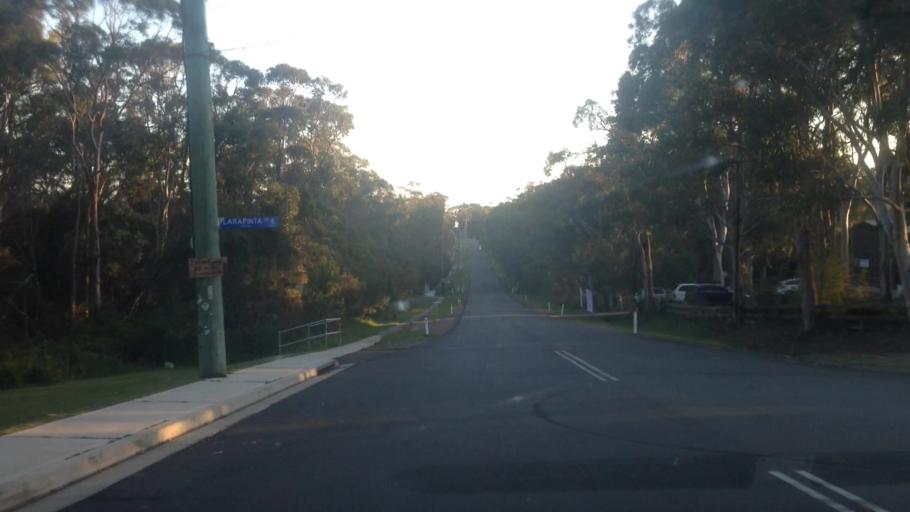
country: AU
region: New South Wales
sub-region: Wyong Shire
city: Kingfisher Shores
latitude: -33.1481
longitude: 151.5196
